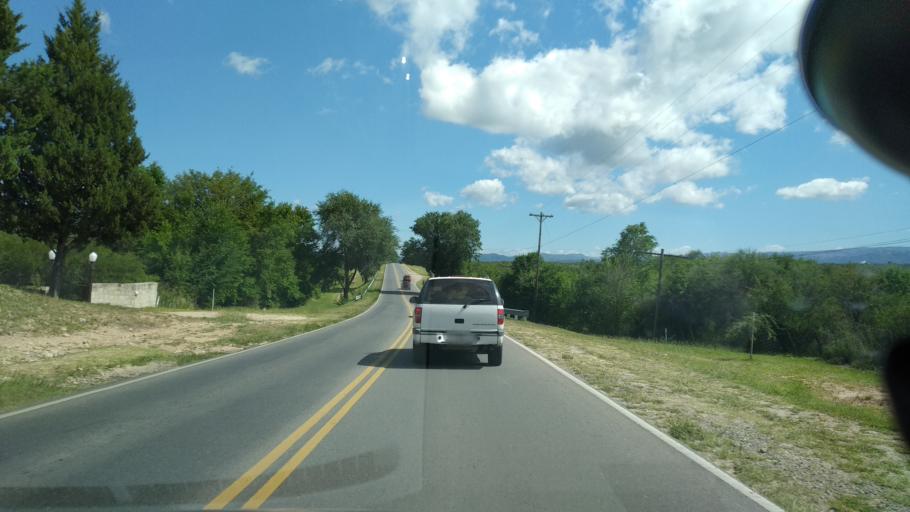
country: AR
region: Cordoba
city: Mina Clavero
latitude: -31.7876
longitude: -64.9980
